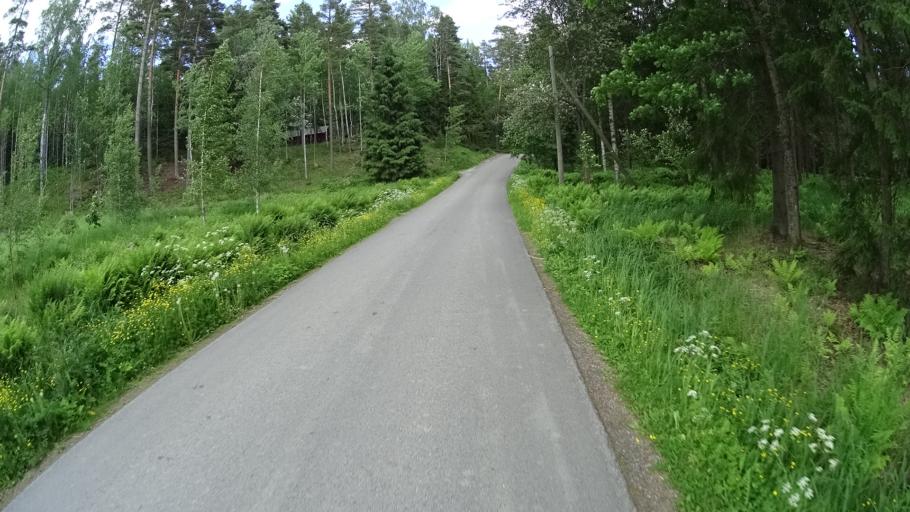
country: FI
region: Uusimaa
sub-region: Helsinki
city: Sibbo
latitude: 60.2587
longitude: 25.3142
